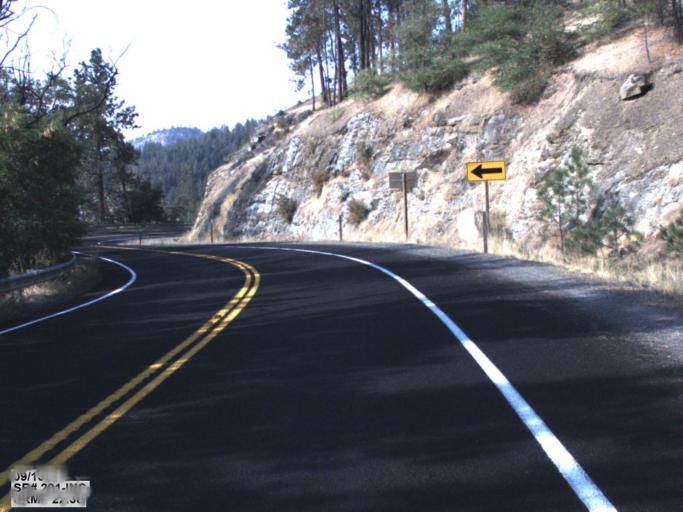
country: US
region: Washington
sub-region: Spokane County
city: Deer Park
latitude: 47.8899
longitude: -117.6870
